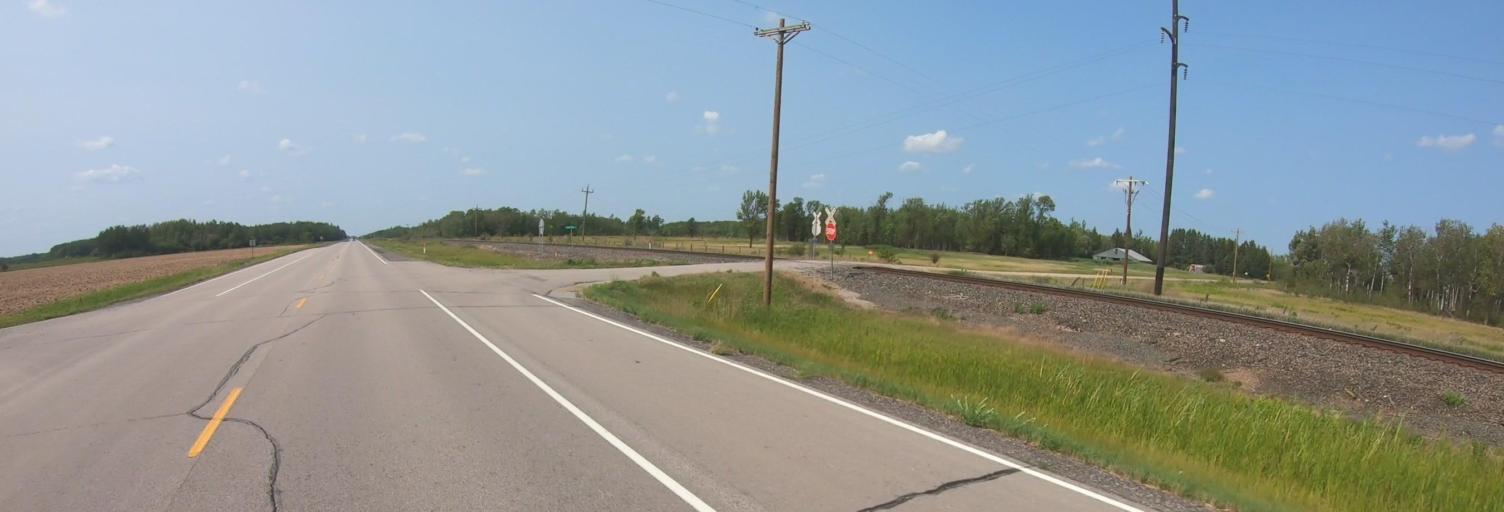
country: US
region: Minnesota
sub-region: Lake of the Woods County
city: Baudette
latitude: 48.7225
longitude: -94.7612
